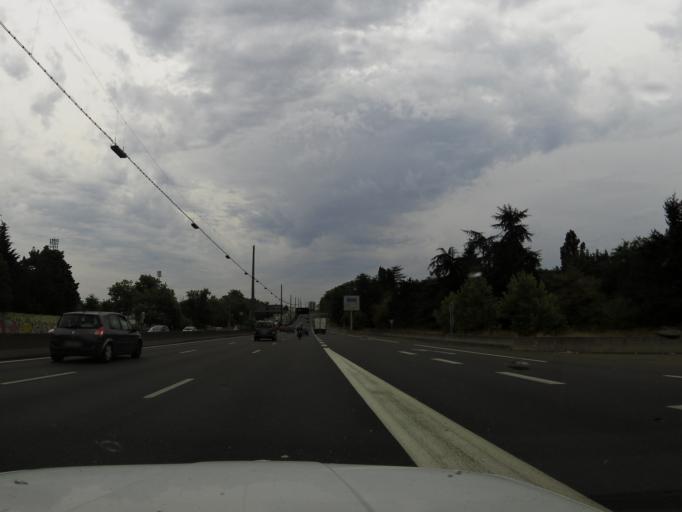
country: FR
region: Rhone-Alpes
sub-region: Departement du Rhone
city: Bron
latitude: 45.7444
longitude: 4.9060
